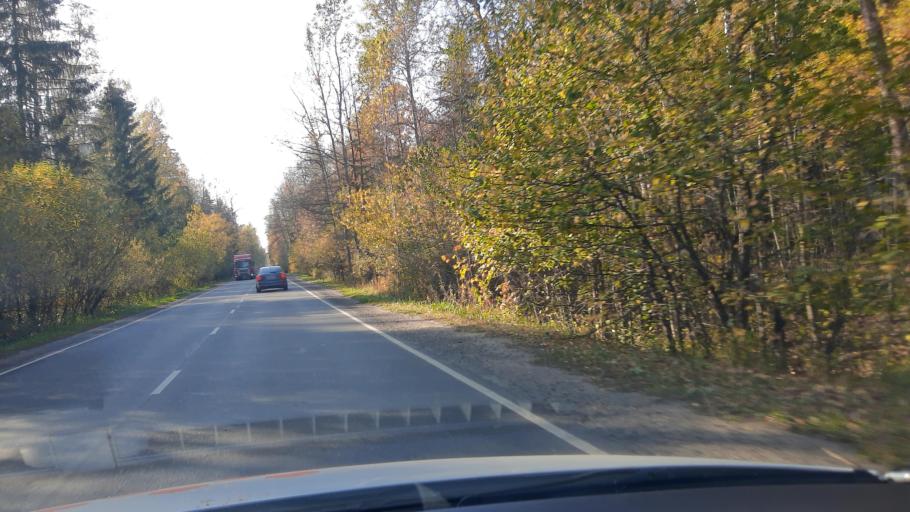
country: RU
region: Moskovskaya
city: Elektrostal'
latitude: 55.8026
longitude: 38.4165
